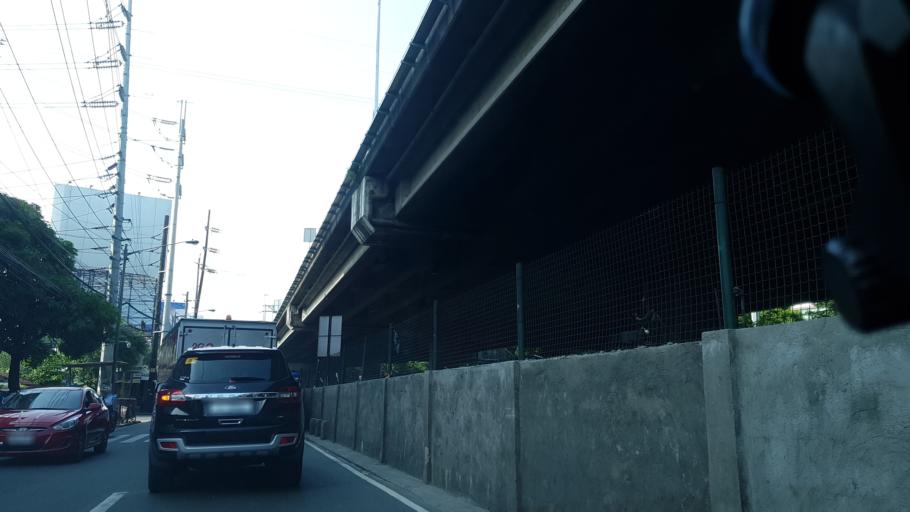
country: PH
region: Calabarzon
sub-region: Province of Rizal
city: Taguig
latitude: 14.4935
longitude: 121.0417
